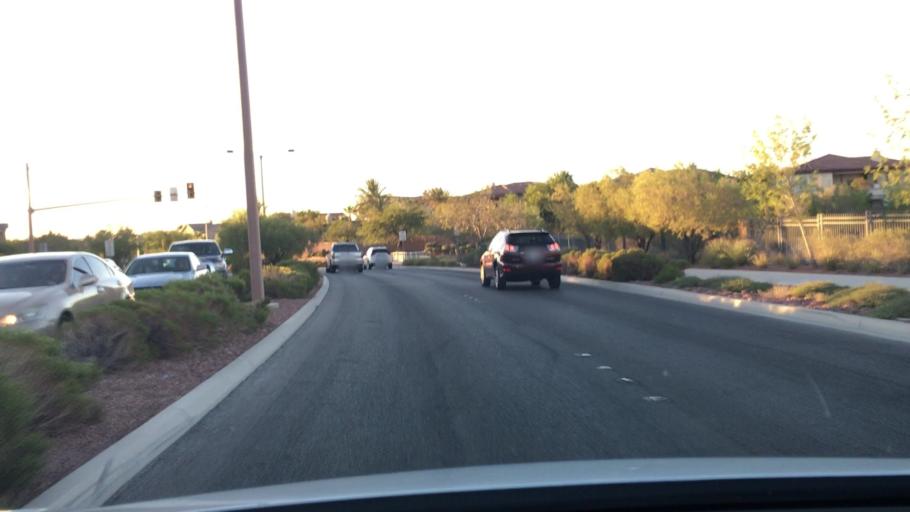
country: US
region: Nevada
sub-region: Clark County
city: Summerlin South
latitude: 36.1567
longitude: -115.3514
